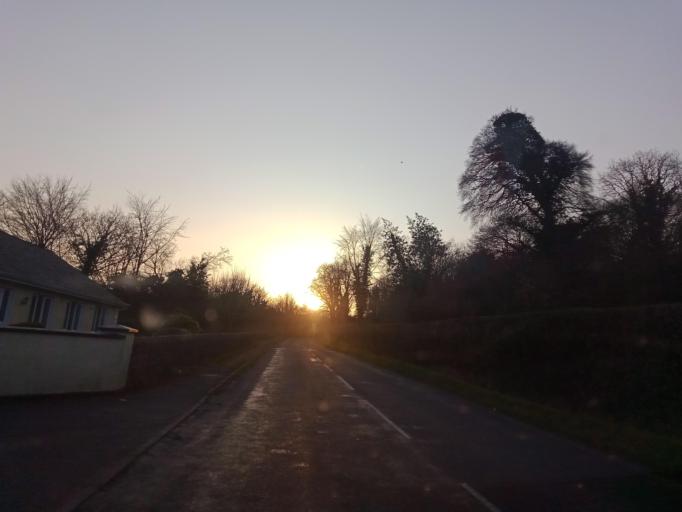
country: IE
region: Leinster
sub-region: Kilkenny
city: Castlecomer
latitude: 52.8080
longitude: -7.2171
